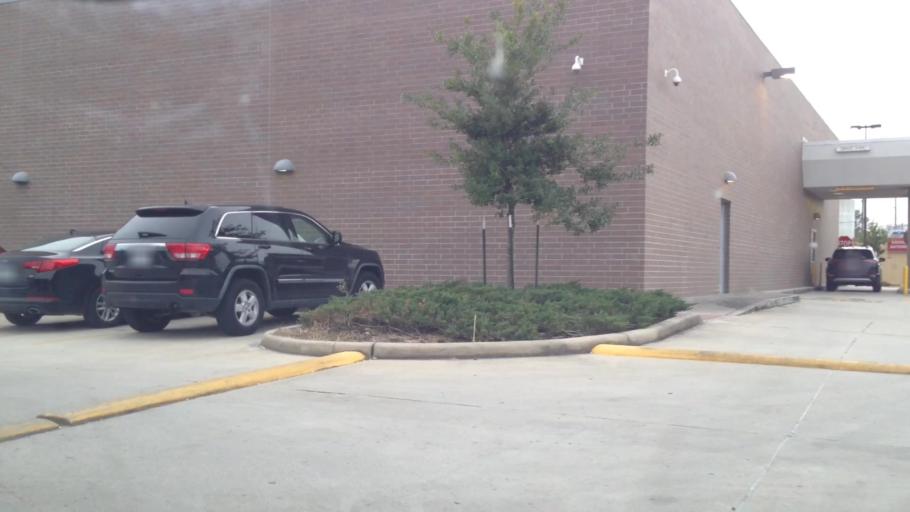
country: US
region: Louisiana
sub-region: Jefferson Parish
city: Metairie Terrace
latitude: 29.9764
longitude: -90.1785
